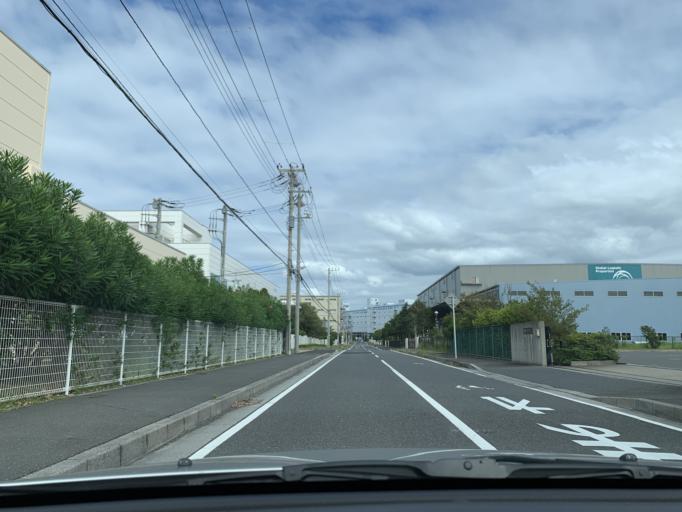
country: JP
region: Tokyo
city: Urayasu
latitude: 35.6209
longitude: 139.8956
